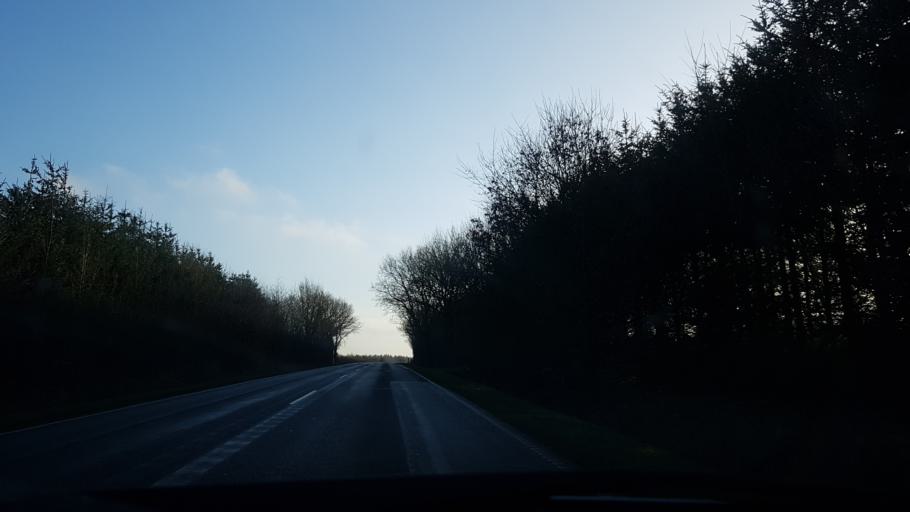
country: DK
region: South Denmark
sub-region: Tonder Kommune
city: Toftlund
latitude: 55.2184
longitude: 9.1814
